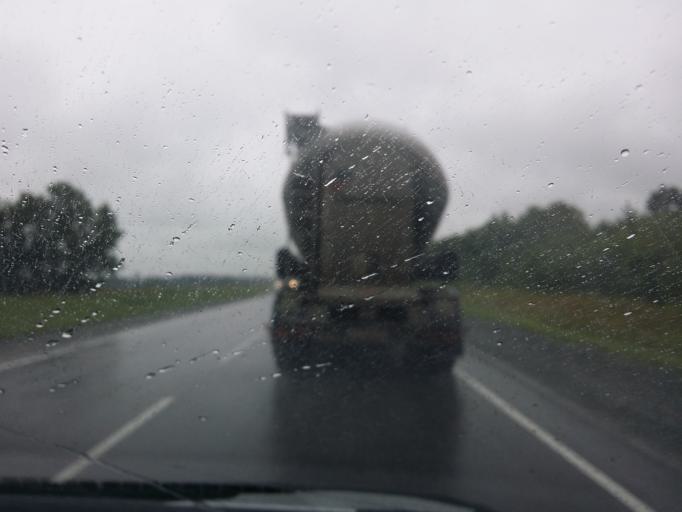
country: RU
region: Altai Krai
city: Bayunovskiye Klyuchi
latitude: 53.3058
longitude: 84.2525
